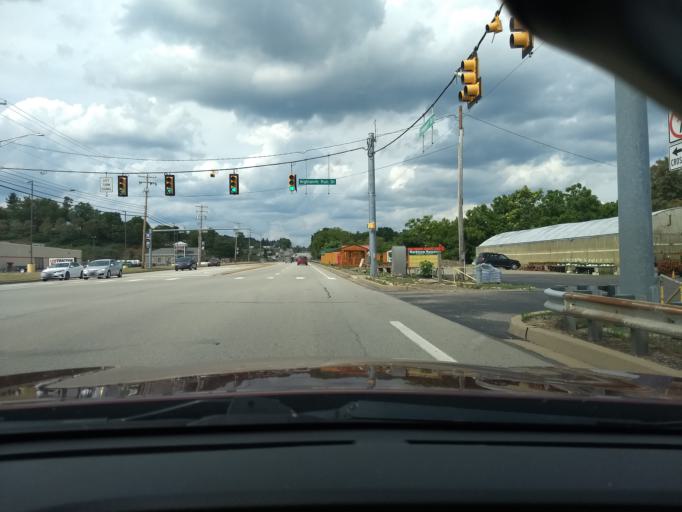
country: US
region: Pennsylvania
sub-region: Armstrong County
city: Freeport
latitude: 40.6459
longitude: -79.7096
